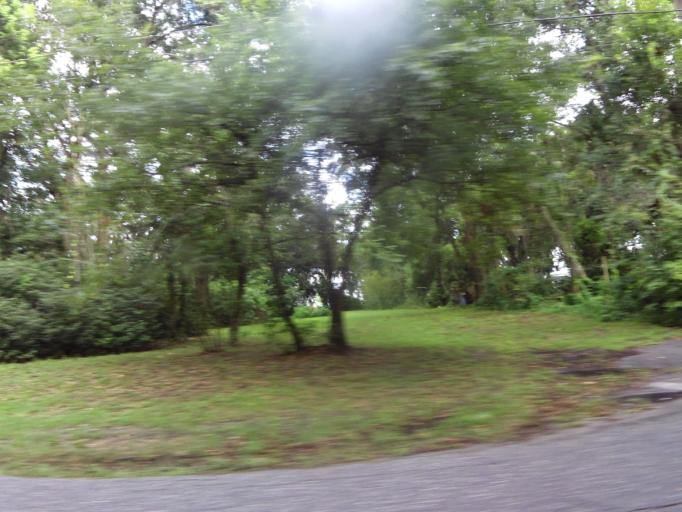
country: US
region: Florida
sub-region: Nassau County
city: Nassau Village-Ratliff
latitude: 30.4333
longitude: -81.7642
